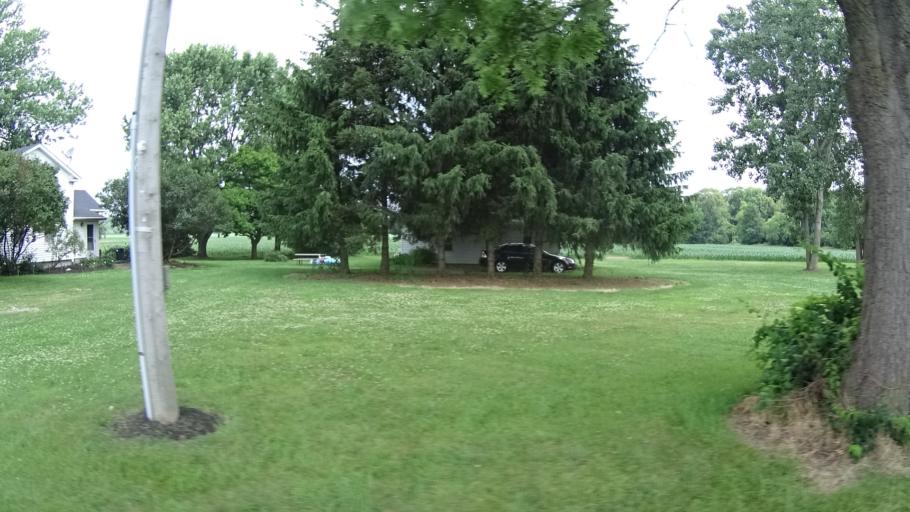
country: US
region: Ohio
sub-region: Lorain County
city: Vermilion
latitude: 41.3771
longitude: -82.3535
